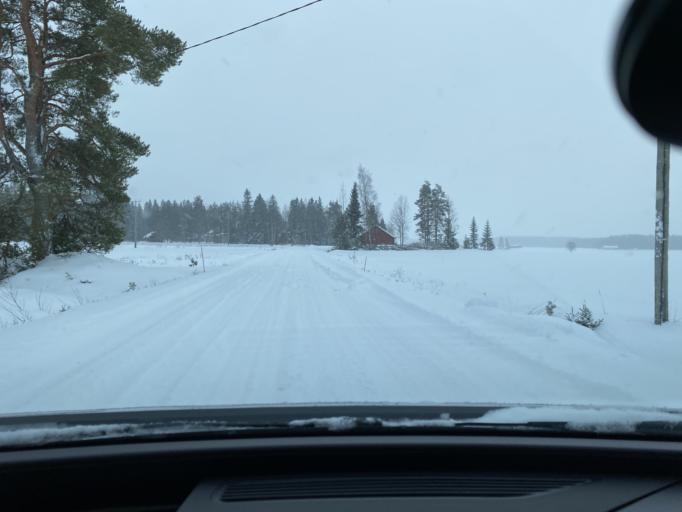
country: FI
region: Haeme
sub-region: Forssa
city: Humppila
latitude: 61.0111
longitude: 23.3030
